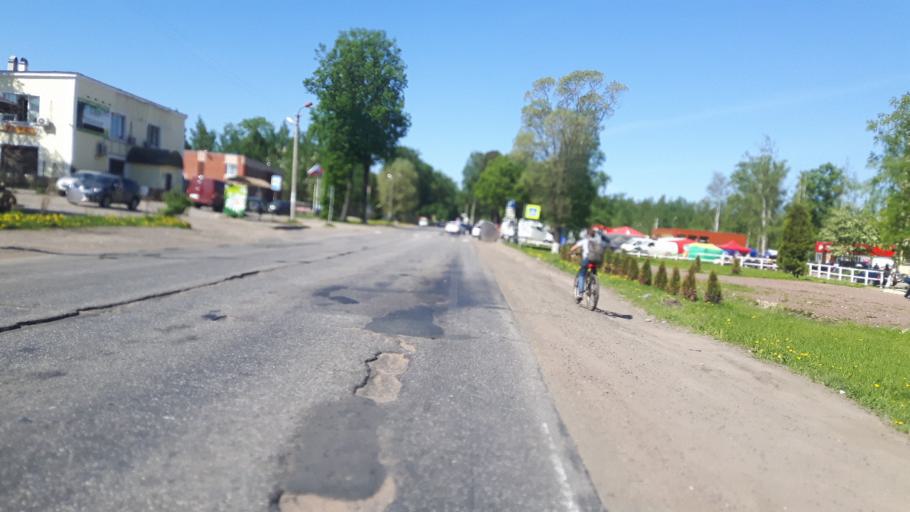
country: RU
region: Leningrad
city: Lebyazh'ye
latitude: 59.9612
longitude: 29.4198
